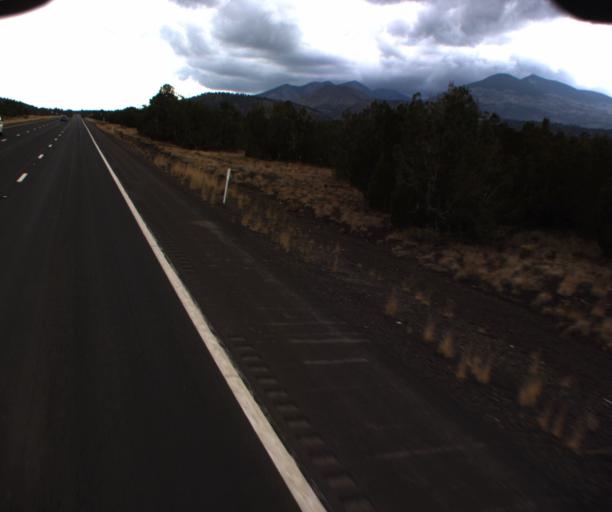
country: US
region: Arizona
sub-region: Coconino County
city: Flagstaff
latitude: 35.4095
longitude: -111.5740
